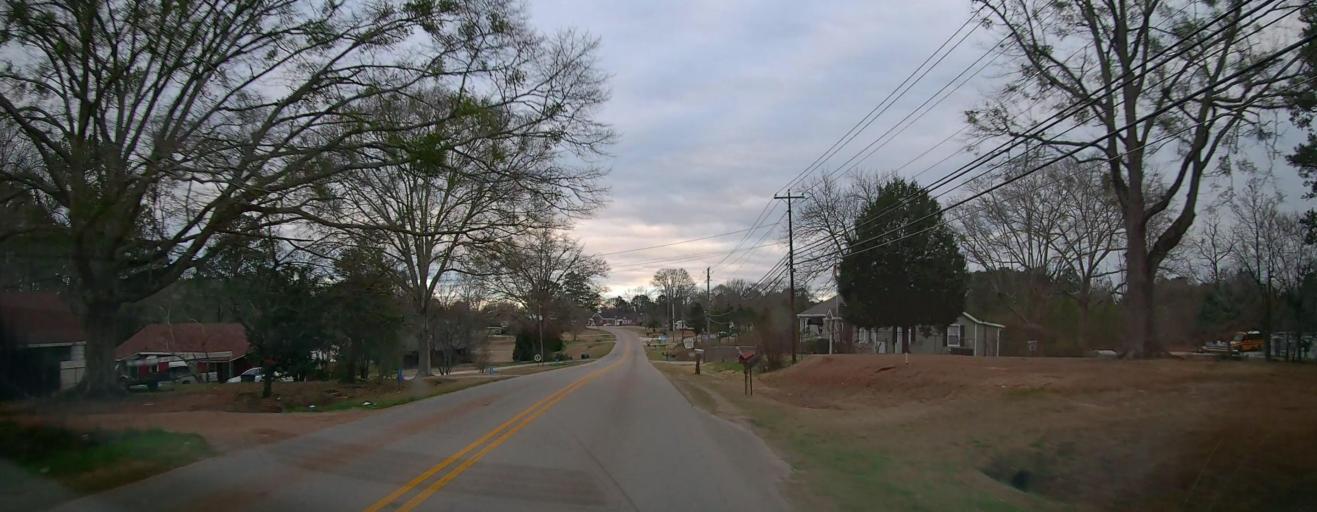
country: US
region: Alabama
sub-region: Chambers County
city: Huguley
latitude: 32.8415
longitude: -85.2329
